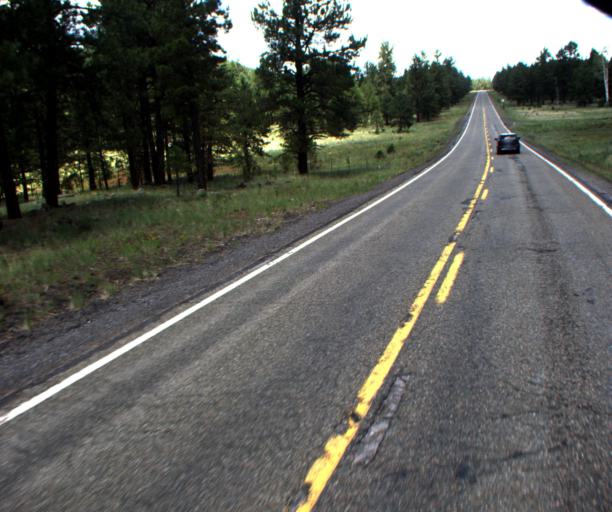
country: US
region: Arizona
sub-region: Coconino County
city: Parks
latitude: 35.3566
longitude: -111.7908
